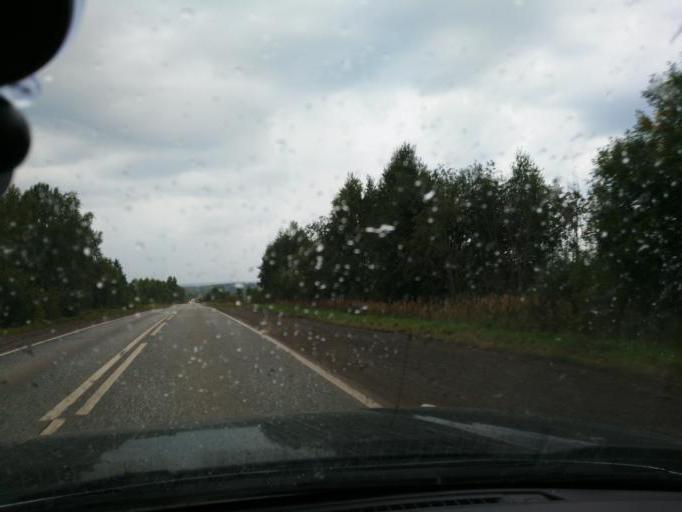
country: RU
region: Perm
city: Chernushka
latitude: 56.8460
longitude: 55.9652
